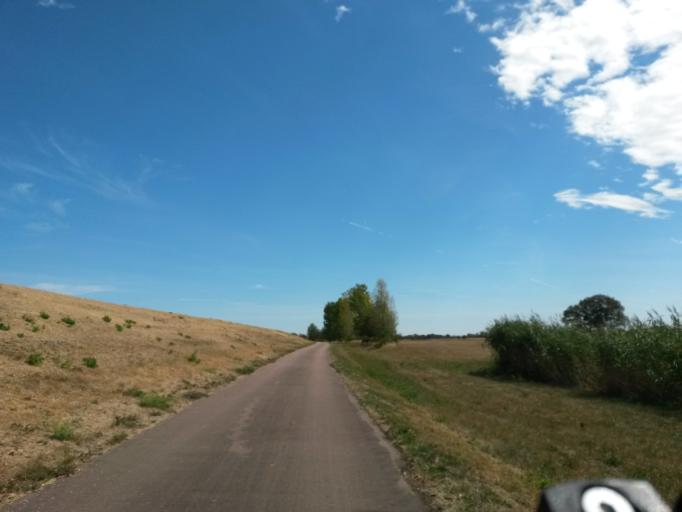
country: DE
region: Saxony-Anhalt
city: Bergwitz
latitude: 51.8536
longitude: 12.5577
